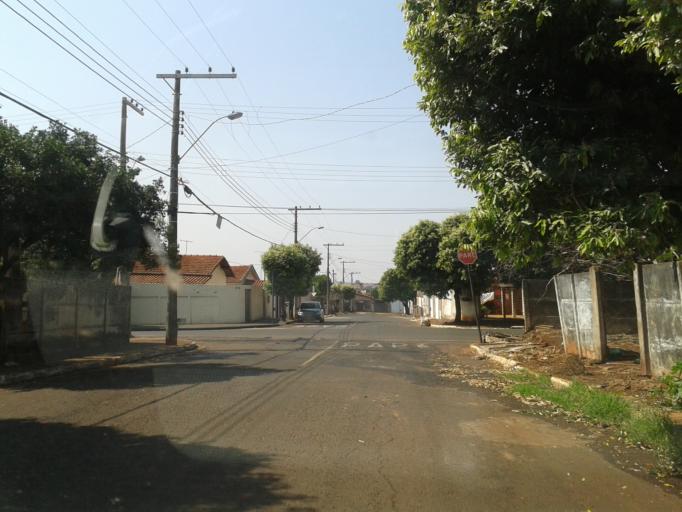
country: BR
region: Minas Gerais
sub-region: Ituiutaba
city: Ituiutaba
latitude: -18.9720
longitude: -49.4746
